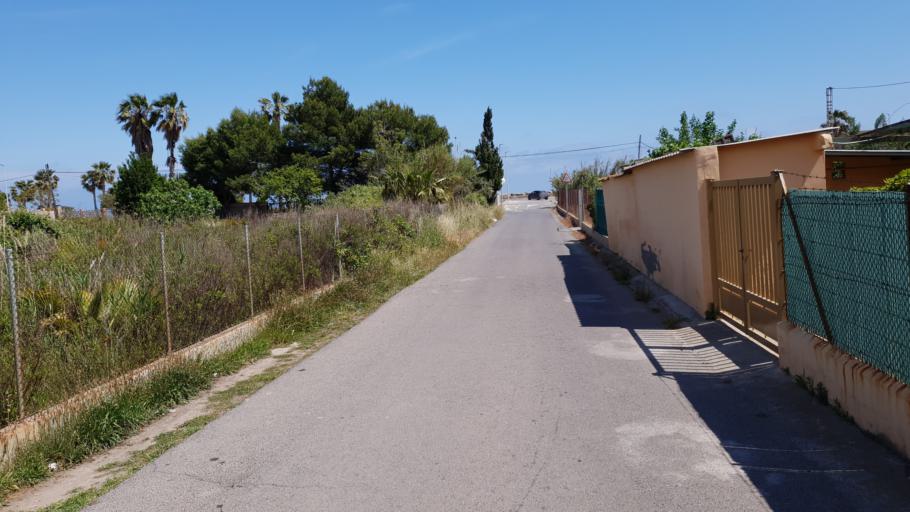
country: ES
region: Valencia
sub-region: Provincia de Castello
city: Burriana
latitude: 39.8582
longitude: -0.0867
